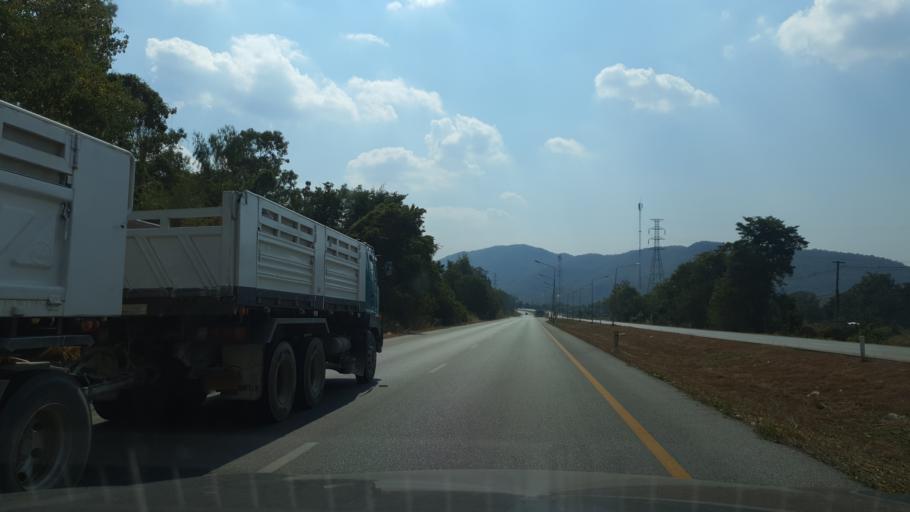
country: TH
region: Lampang
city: Mae Phrik
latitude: 17.3707
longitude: 99.1484
